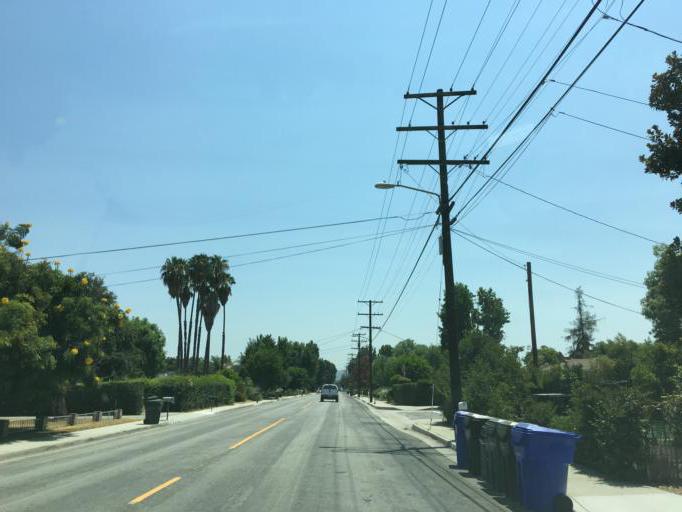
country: US
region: California
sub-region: Los Angeles County
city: Mayflower Village
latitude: 34.1173
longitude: -118.0124
